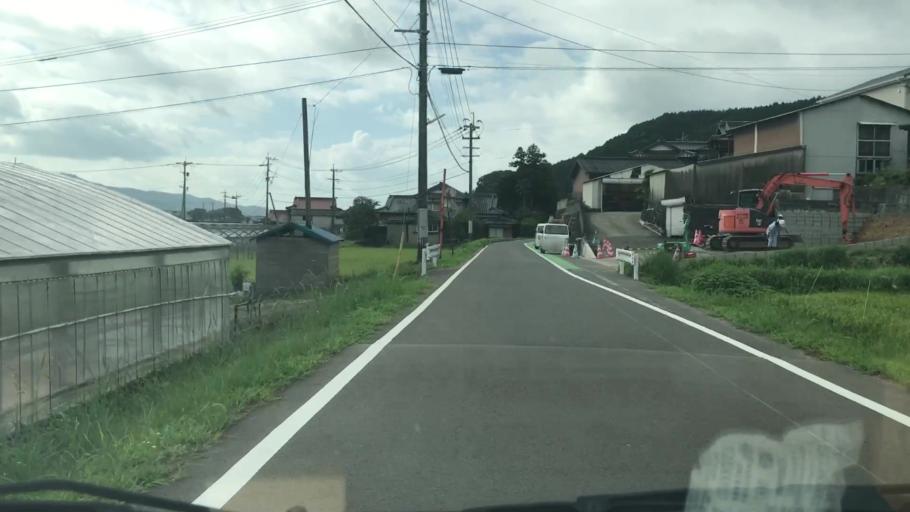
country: JP
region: Saga Prefecture
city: Takeocho-takeo
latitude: 33.2240
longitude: 130.0237
